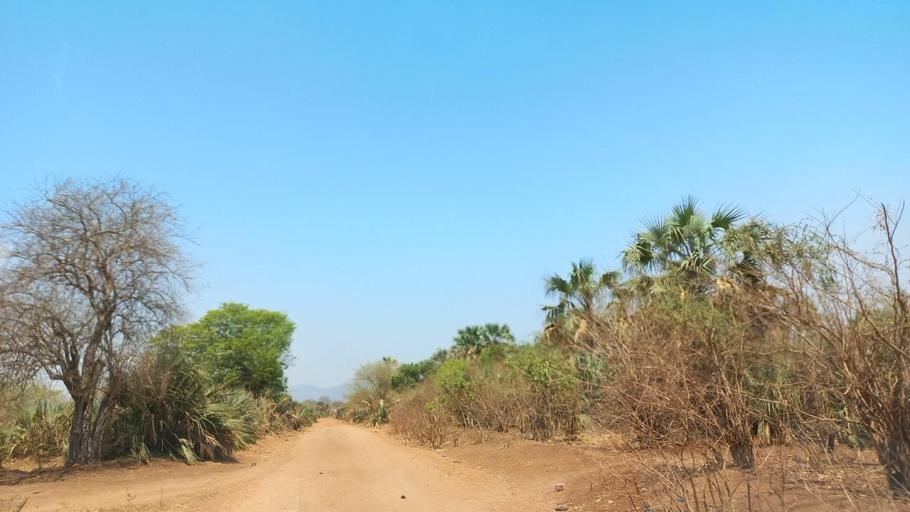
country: ZM
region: Lusaka
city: Luangwa
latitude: -15.1870
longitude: 30.2102
